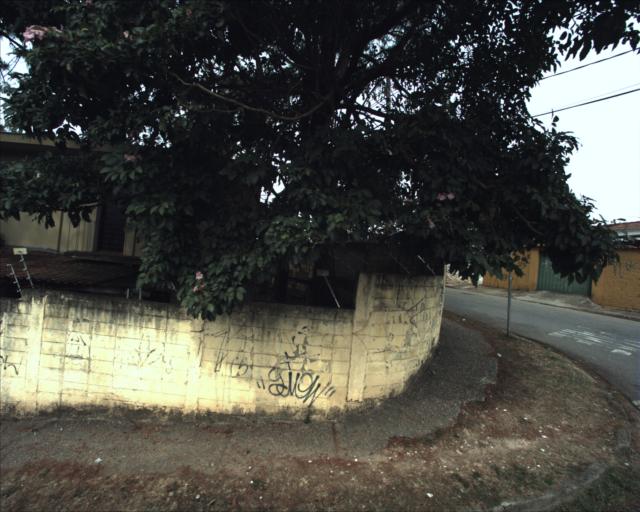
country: BR
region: Sao Paulo
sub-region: Sorocaba
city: Sorocaba
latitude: -23.4846
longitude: -47.4666
